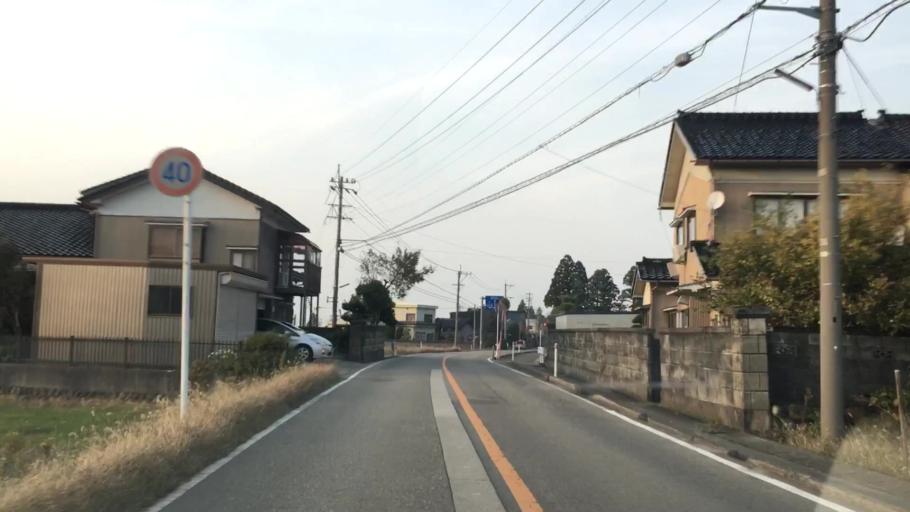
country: JP
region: Toyama
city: Toyama-shi
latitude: 36.6093
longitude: 137.2519
